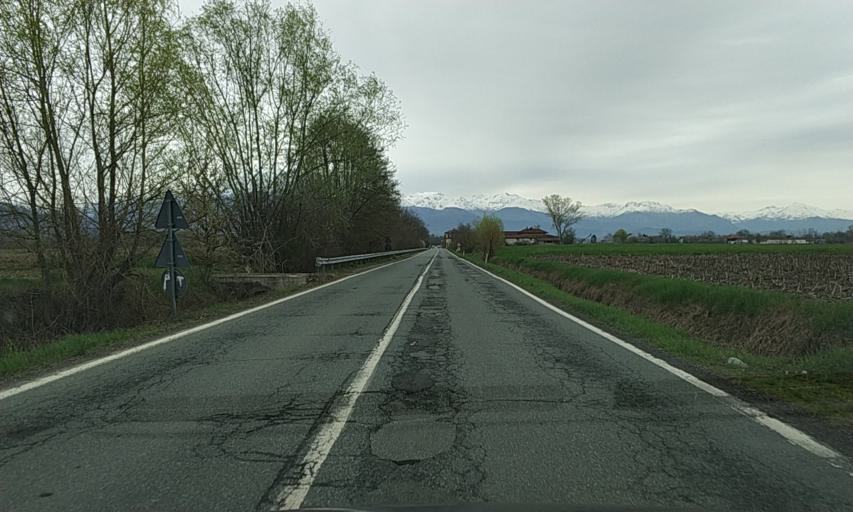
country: IT
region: Piedmont
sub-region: Provincia di Torino
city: Front
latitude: 45.3044
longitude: 7.6777
